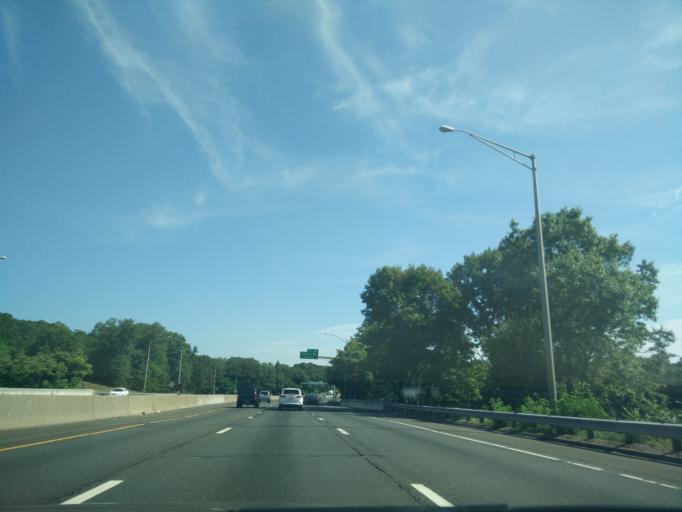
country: US
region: Connecticut
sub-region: New Haven County
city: City of Milford (balance)
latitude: 41.2123
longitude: -73.0887
